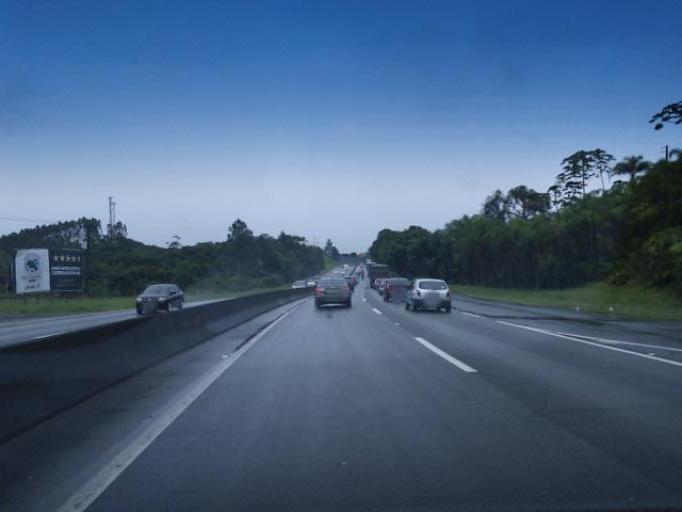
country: BR
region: Santa Catarina
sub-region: Joinville
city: Joinville
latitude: -26.4465
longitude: -48.7941
